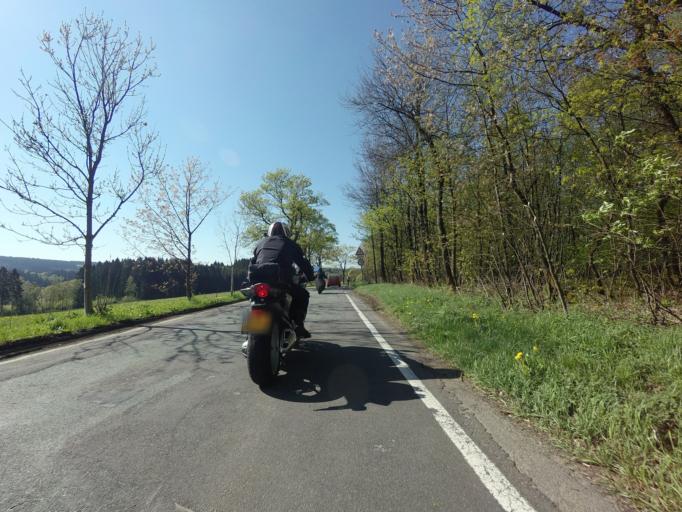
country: DE
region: North Rhine-Westphalia
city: Meinerzhagen
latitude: 51.1479
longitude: 7.6766
